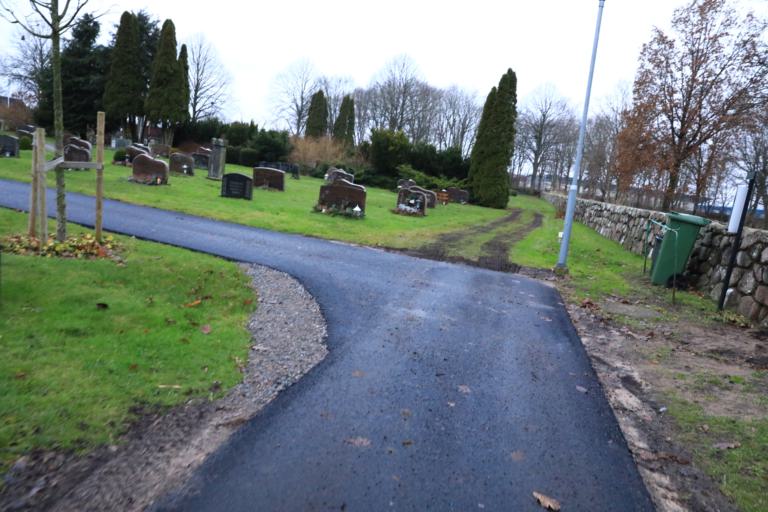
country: SE
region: Halland
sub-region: Varbergs Kommun
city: Tvaaker
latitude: 57.0474
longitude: 12.3997
